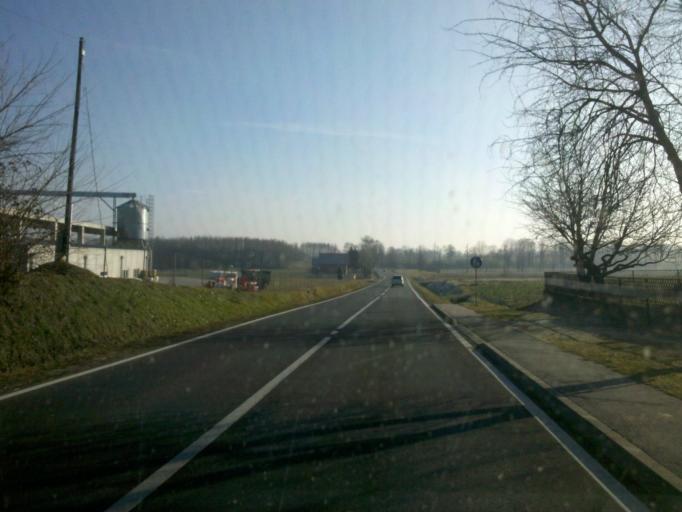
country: HR
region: Koprivnicko-Krizevacka
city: Peteranec
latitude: 46.1138
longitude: 16.8901
